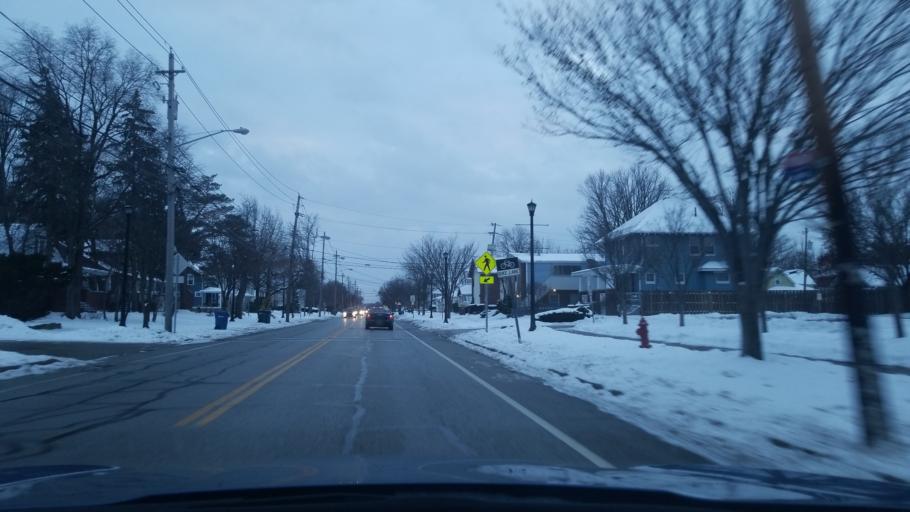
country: US
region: Ohio
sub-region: Cuyahoga County
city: Berea
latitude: 41.3780
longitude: -81.8531
